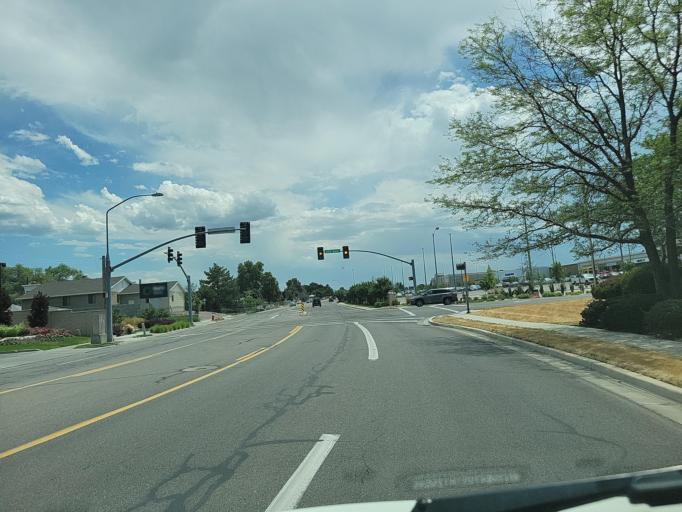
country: US
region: Utah
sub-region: Salt Lake County
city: Murray
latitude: 40.6388
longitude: -111.8831
